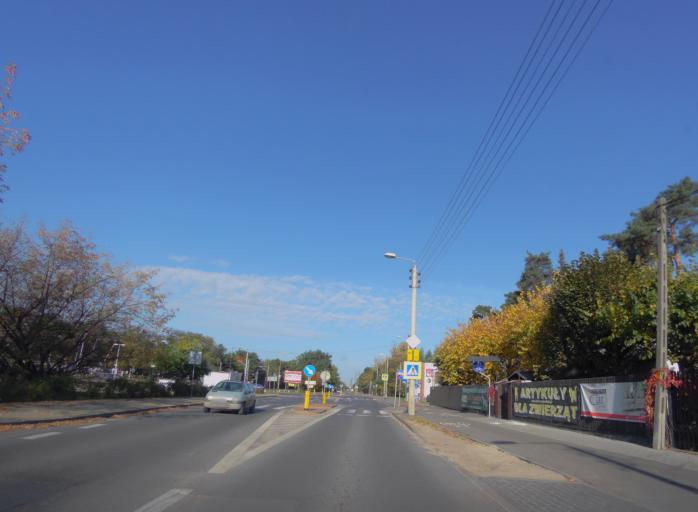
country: PL
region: Masovian Voivodeship
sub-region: Powiat otwocki
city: Jozefow
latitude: 52.1486
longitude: 21.2248
